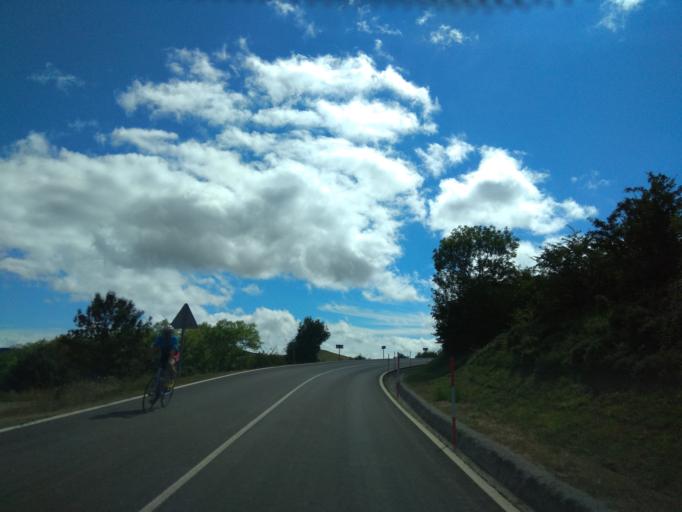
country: ES
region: Cantabria
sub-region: Provincia de Cantabria
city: Villaescusa
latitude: 42.9597
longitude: -4.1649
